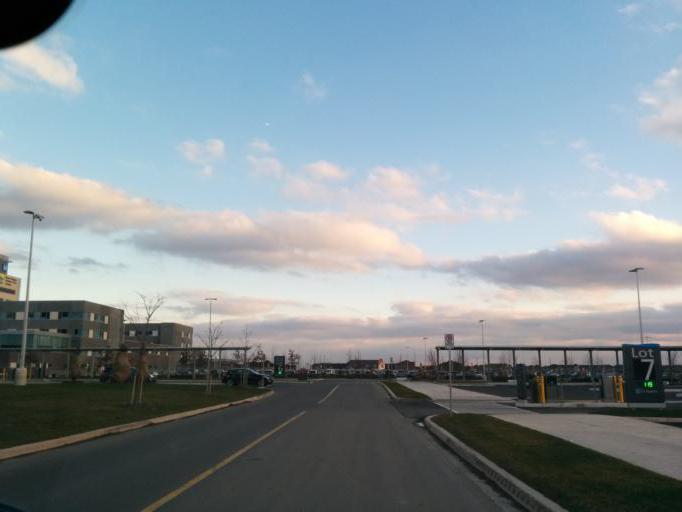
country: CA
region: Ontario
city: Oakville
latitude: 43.4504
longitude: -79.7667
